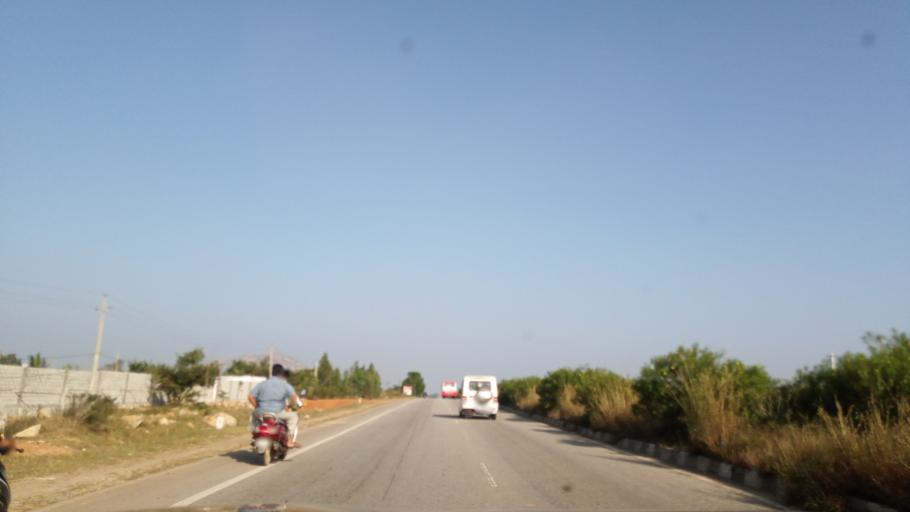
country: IN
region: Karnataka
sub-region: Kolar
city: Mulbagal
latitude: 13.1551
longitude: 78.3381
